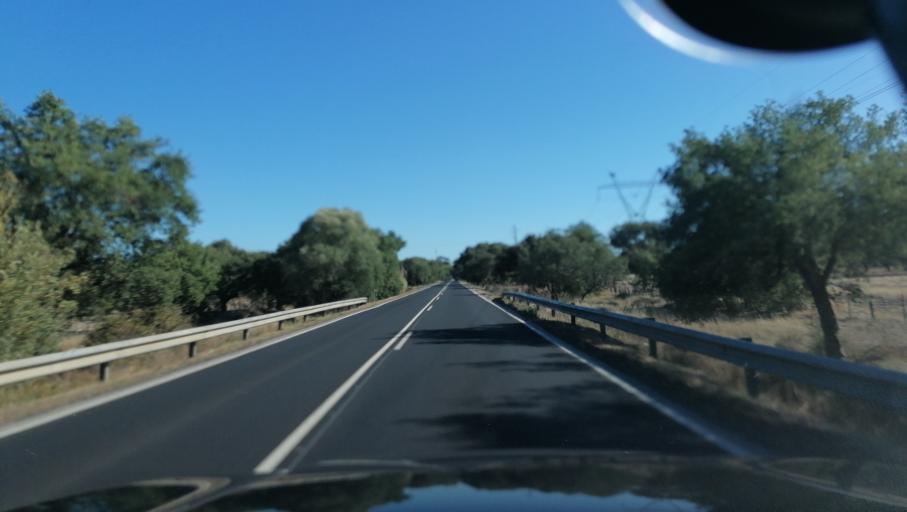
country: PT
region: Santarem
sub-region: Benavente
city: Poceirao
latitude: 38.8430
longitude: -8.8810
